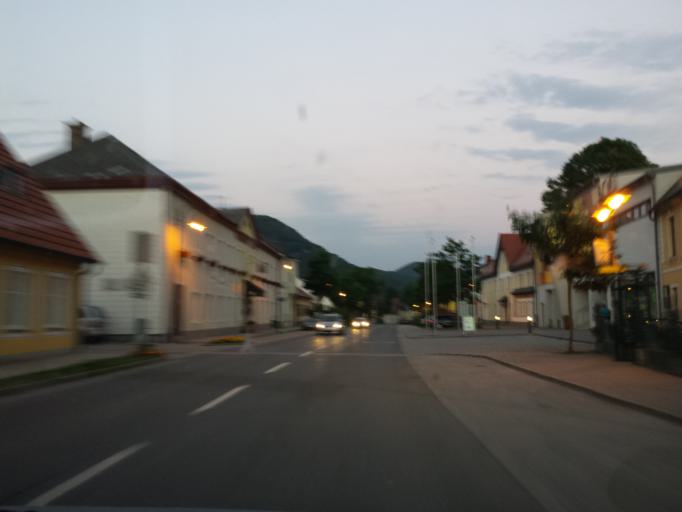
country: AT
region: Lower Austria
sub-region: Politischer Bezirk Baden
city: Altenmarkt an der Triesting
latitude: 48.0157
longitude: 15.9944
